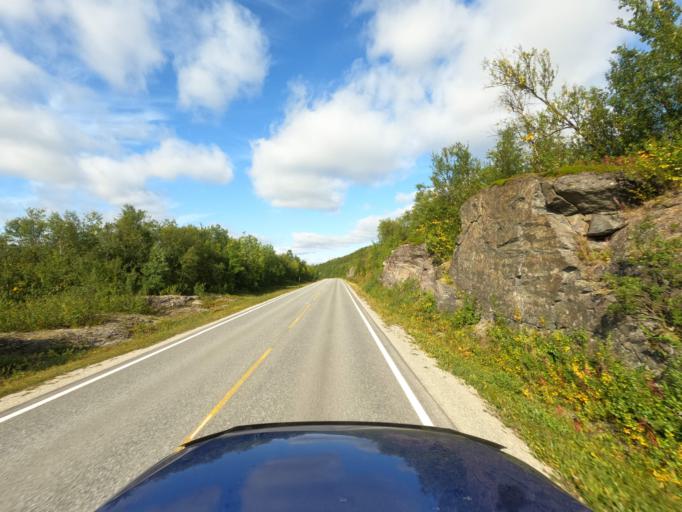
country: NO
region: Finnmark Fylke
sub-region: Porsanger
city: Lakselv
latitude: 69.9355
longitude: 24.9750
